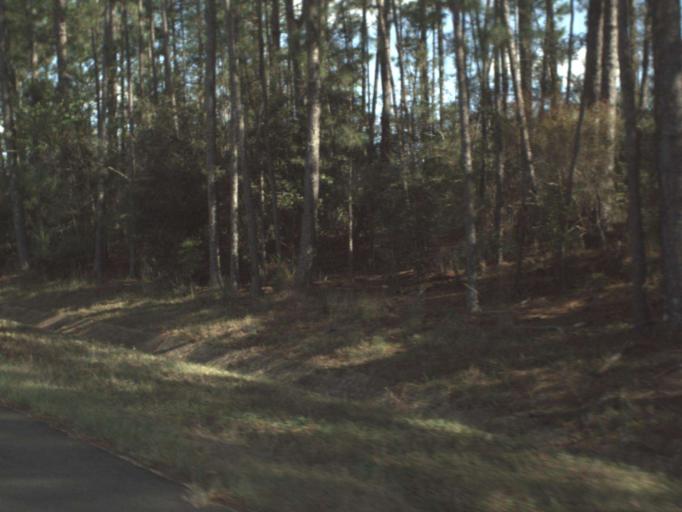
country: US
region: Florida
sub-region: Holmes County
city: Bonifay
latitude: 30.7875
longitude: -85.7621
